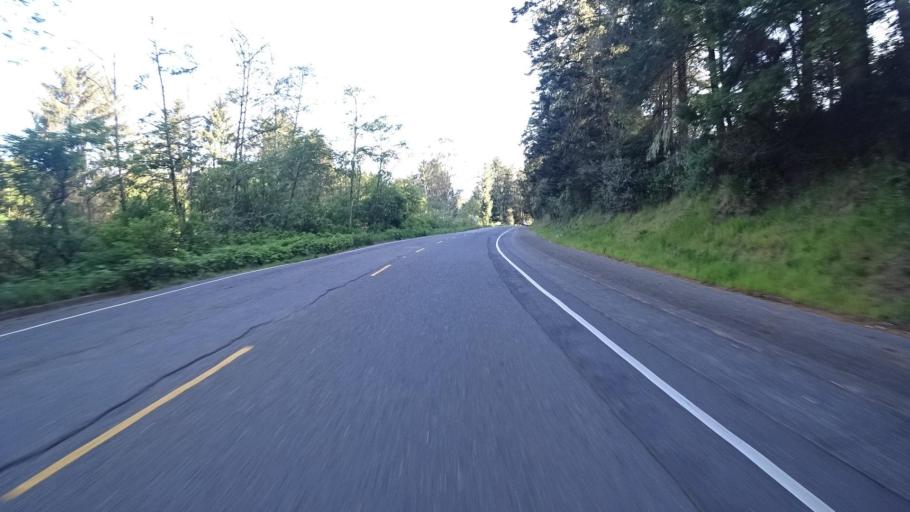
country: US
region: California
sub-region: Humboldt County
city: Humboldt Hill
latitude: 40.7269
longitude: -124.2027
